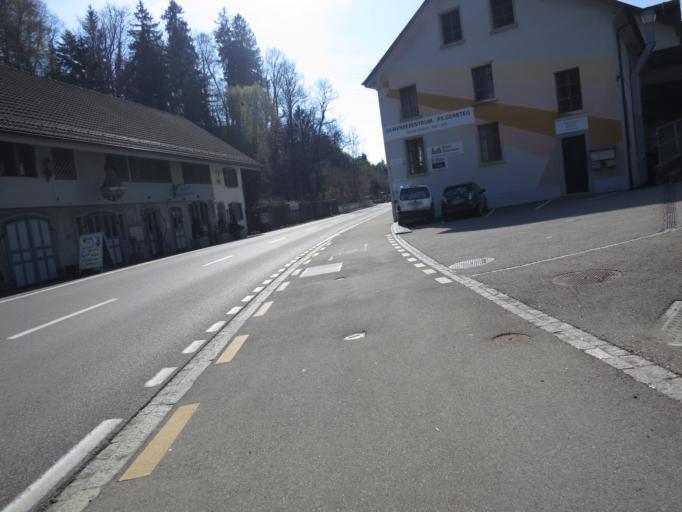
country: CH
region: Zurich
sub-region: Bezirk Hinwil
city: Rueti / Oberdorf
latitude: 47.2697
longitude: 8.8788
